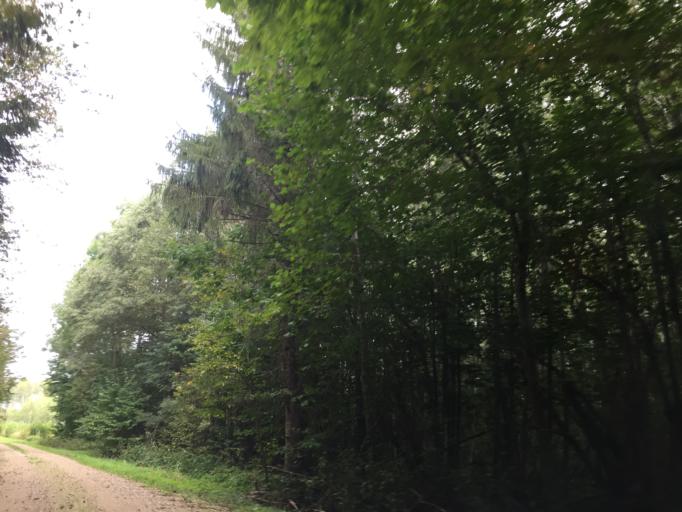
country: LV
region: Pargaujas
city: Stalbe
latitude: 57.4795
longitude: 24.9076
